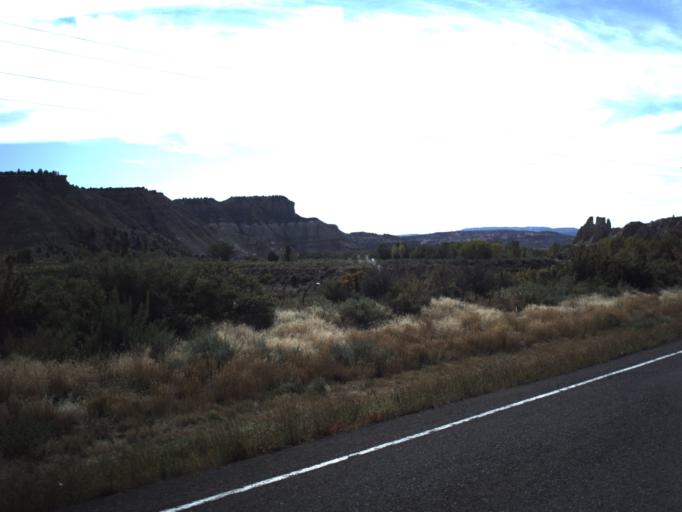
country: US
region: Utah
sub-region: Garfield County
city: Panguitch
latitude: 37.5971
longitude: -112.0617
